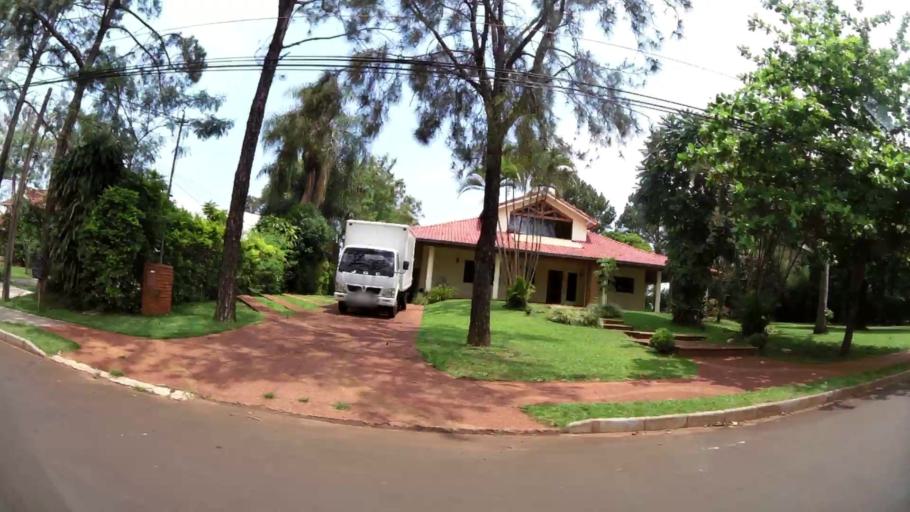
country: PY
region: Alto Parana
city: Ciudad del Este
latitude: -25.4907
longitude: -54.6138
